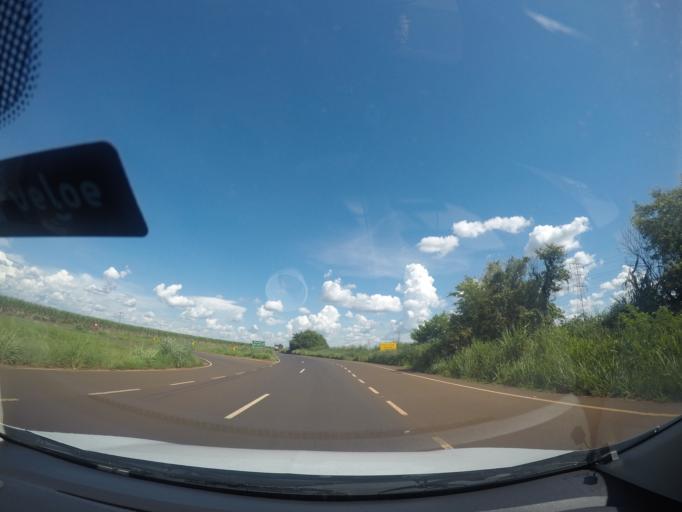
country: BR
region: Sao Paulo
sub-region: Barretos
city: Barretos
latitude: -20.3038
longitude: -48.6659
